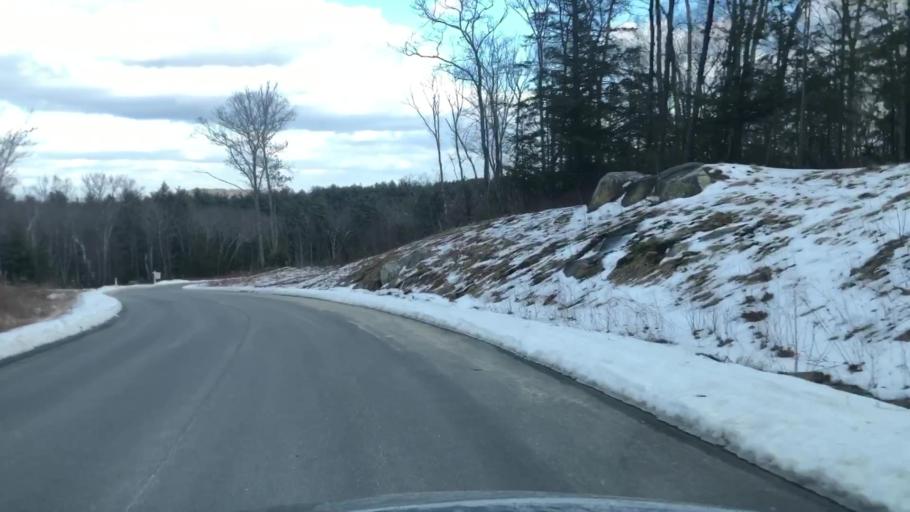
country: US
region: New Hampshire
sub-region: Hillsborough County
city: Milford
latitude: 42.8534
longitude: -71.6419
